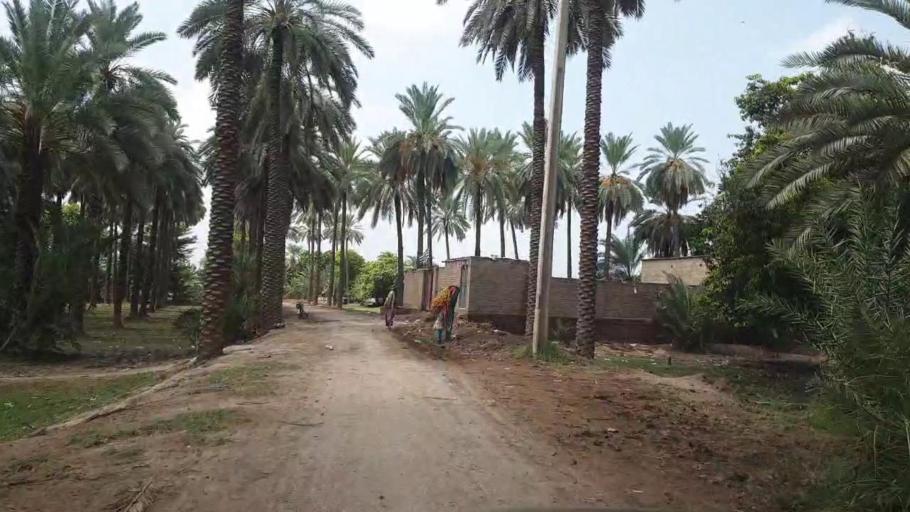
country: PK
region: Sindh
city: Pir jo Goth
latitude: 27.6140
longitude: 68.6751
